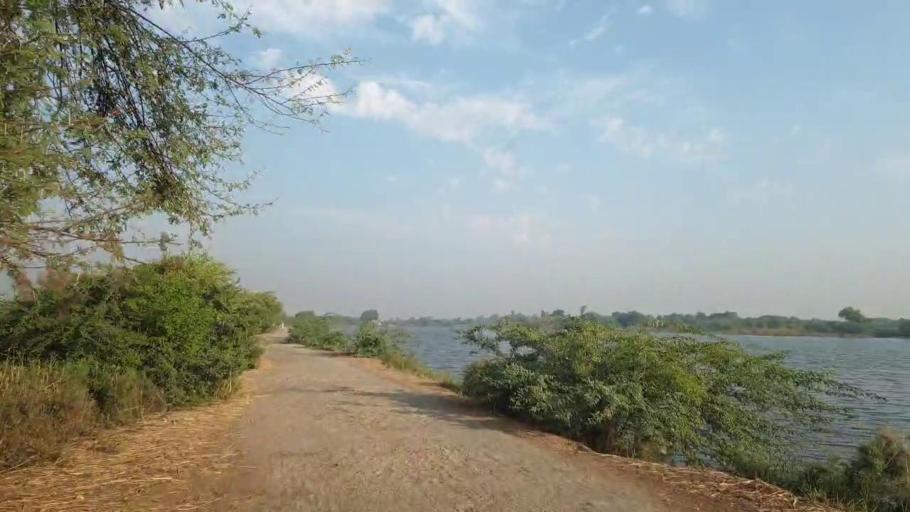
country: PK
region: Sindh
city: Tando Bago
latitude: 24.7996
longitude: 68.9602
